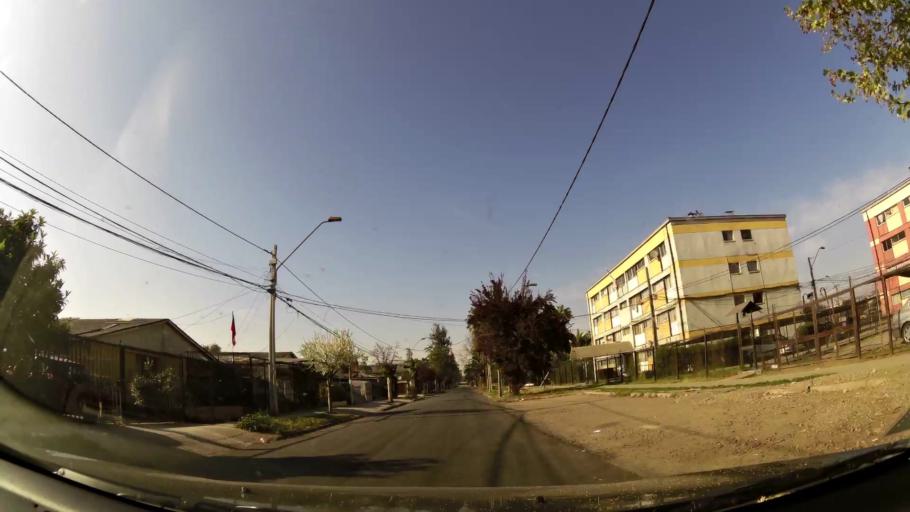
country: CL
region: Santiago Metropolitan
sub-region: Provincia de Santiago
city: Santiago
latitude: -33.3875
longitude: -70.6666
